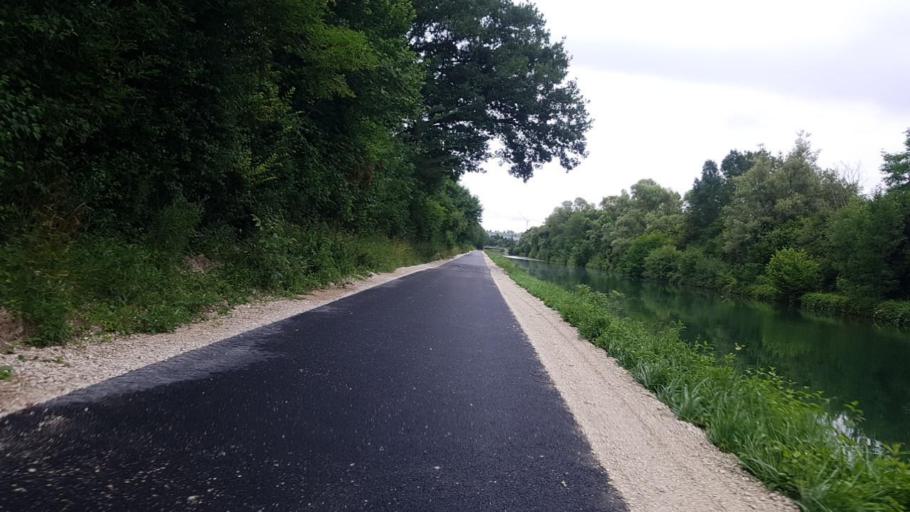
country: FR
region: Champagne-Ardenne
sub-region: Departement de la Marne
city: Vitry-le-Francois
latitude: 48.8283
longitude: 4.5137
